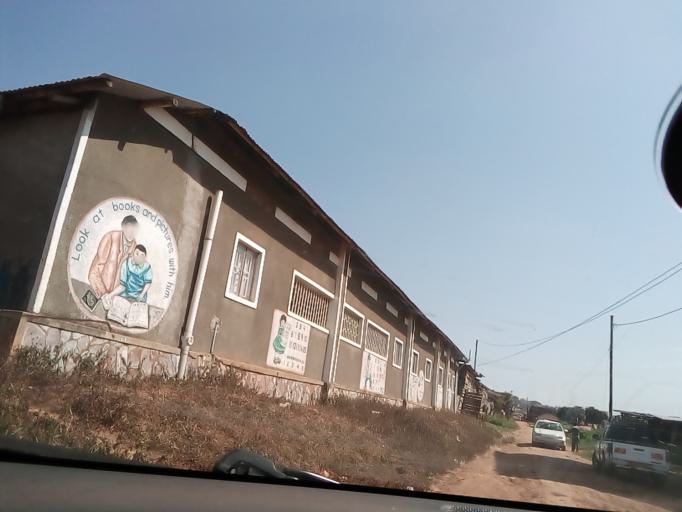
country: UG
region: Central Region
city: Masaka
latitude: -0.3465
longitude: 31.7415
